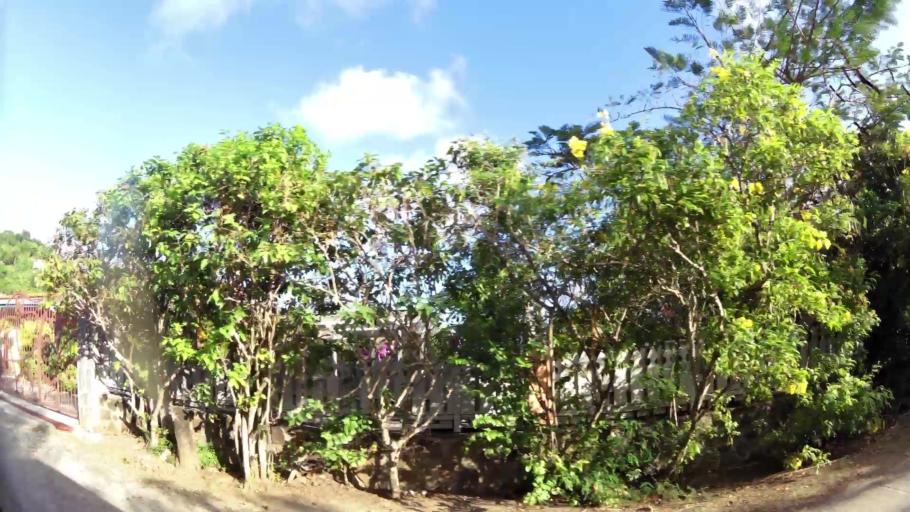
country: LC
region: Gros-Islet
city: Gros Islet
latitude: 14.1027
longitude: -60.9422
